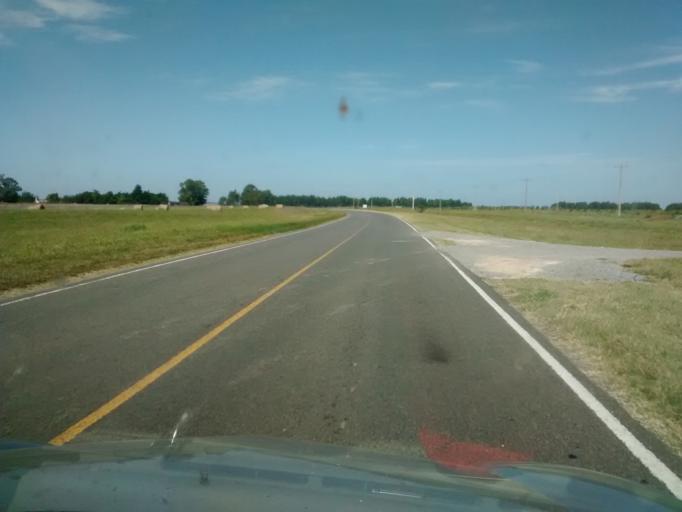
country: AR
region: Buenos Aires
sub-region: Partido de Balcarce
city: Balcarce
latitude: -37.6417
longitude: -58.4900
